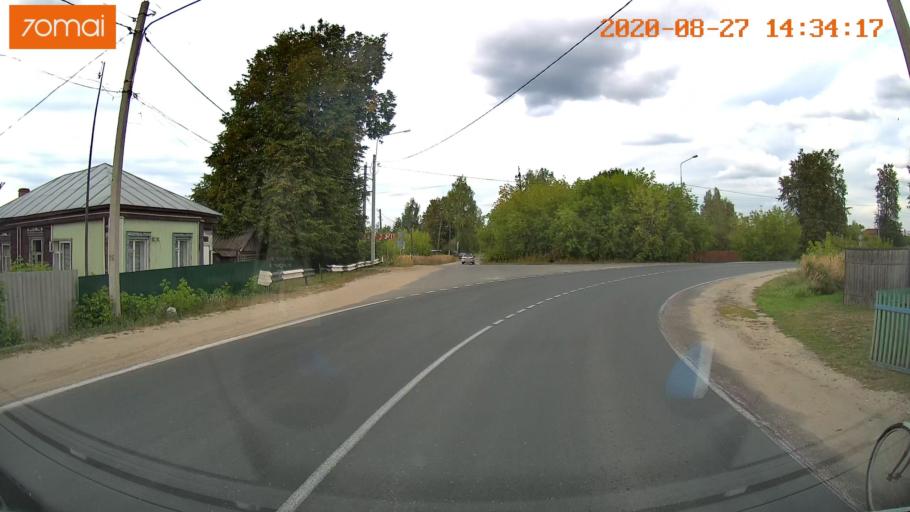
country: RU
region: Rjazan
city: Tuma
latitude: 55.1476
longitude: 40.5504
